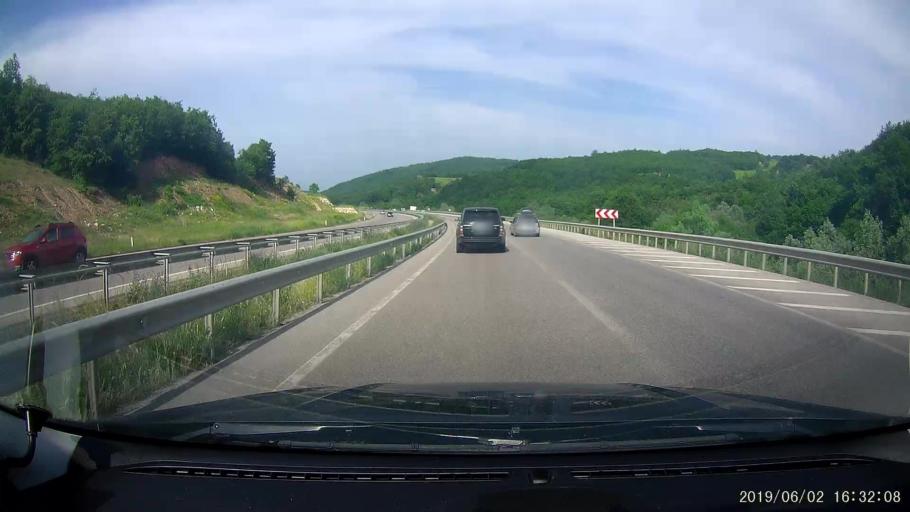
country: TR
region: Samsun
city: Ladik
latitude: 41.0372
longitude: 35.9140
